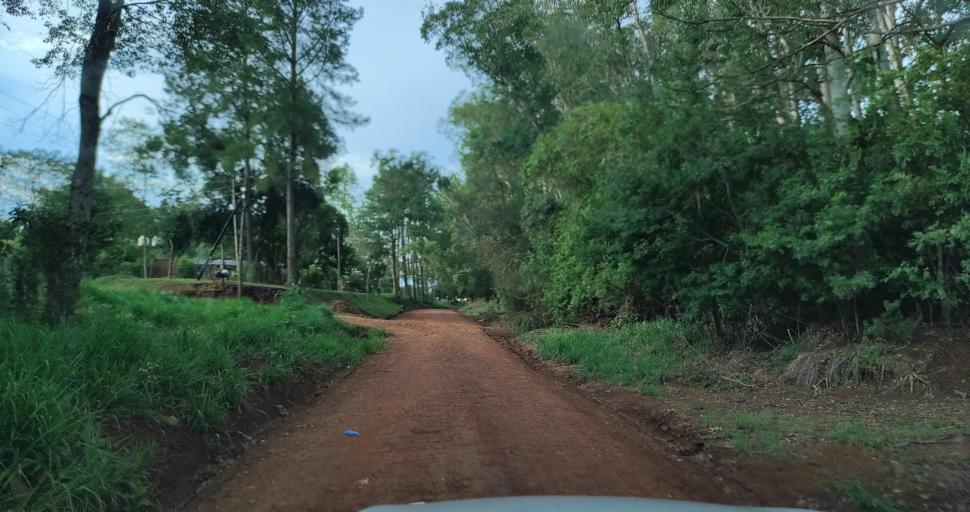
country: AR
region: Misiones
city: Santo Pipo
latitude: -27.1451
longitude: -55.4205
